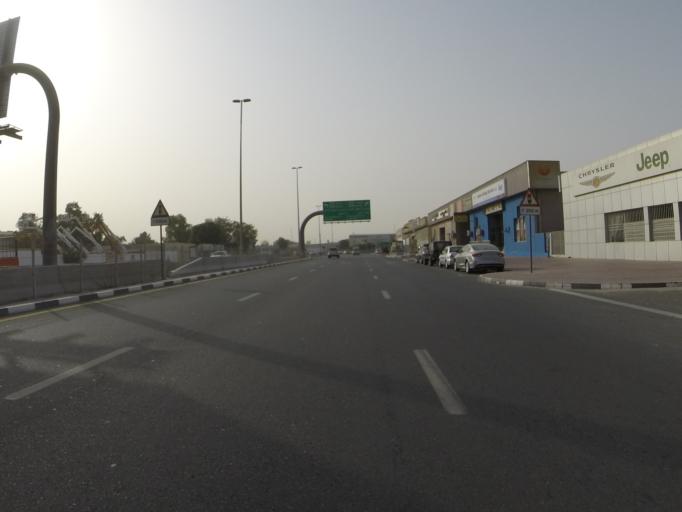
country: AE
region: Dubai
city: Dubai
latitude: 25.1463
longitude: 55.2285
